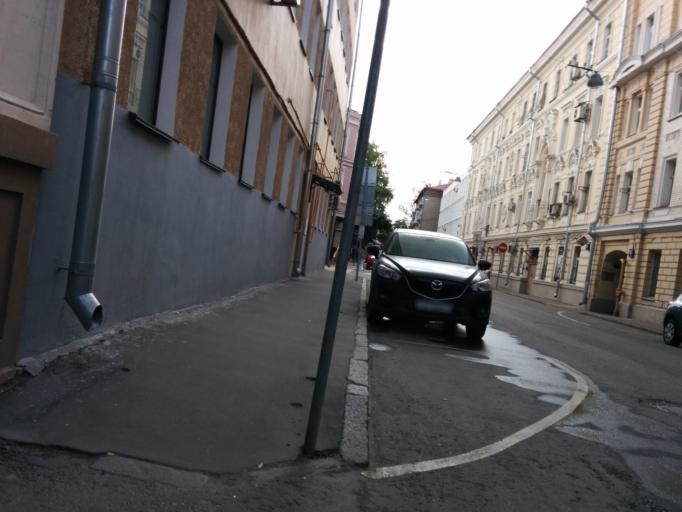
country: RU
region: Moscow
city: Zamoskvorech'ye
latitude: 55.7635
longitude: 37.6468
